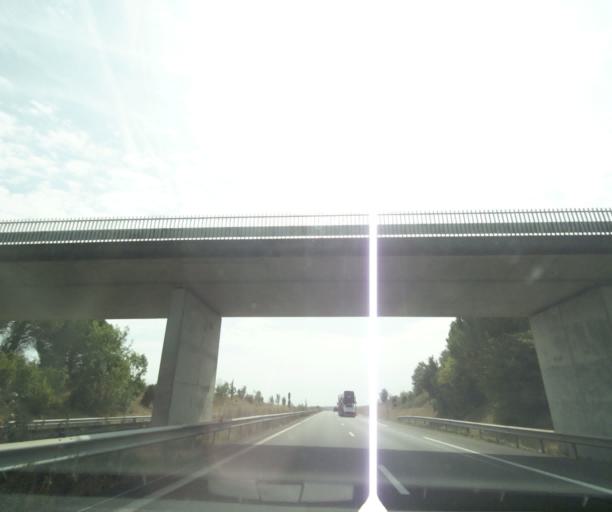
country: FR
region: Poitou-Charentes
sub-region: Departement de la Charente-Maritime
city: Saint-Jean-d'Angely
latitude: 45.9882
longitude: -0.5449
